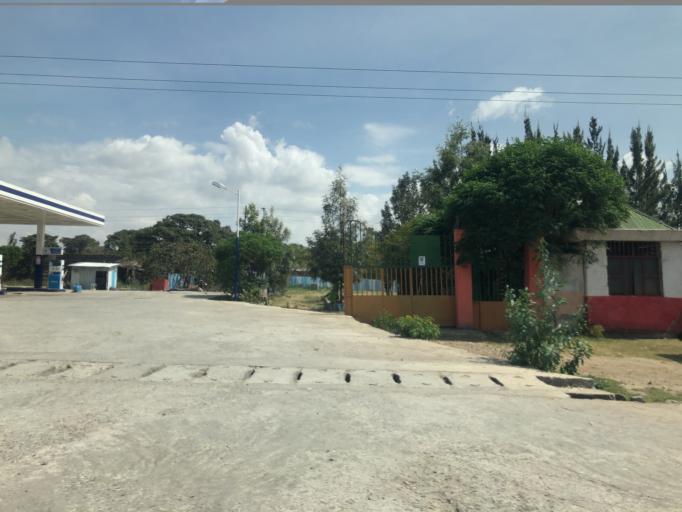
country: ET
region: Oromiya
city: Shashemene
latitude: 7.3126
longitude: 38.6517
